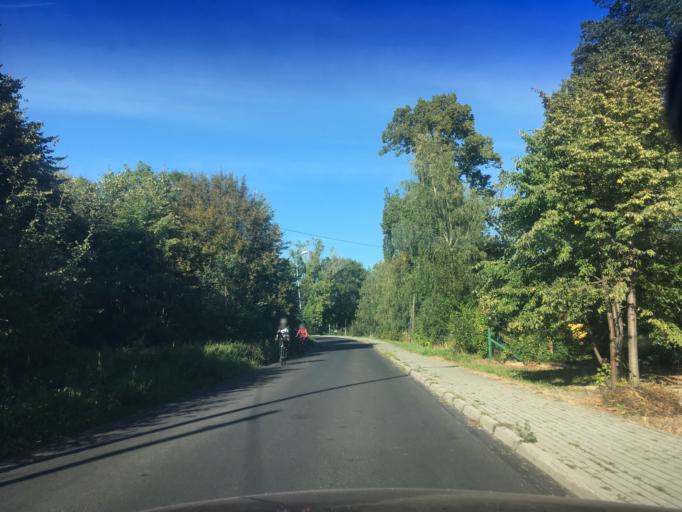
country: PL
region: Lower Silesian Voivodeship
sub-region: Powiat lubanski
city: Swieradow-Zdroj
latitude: 50.9341
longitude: 15.3013
